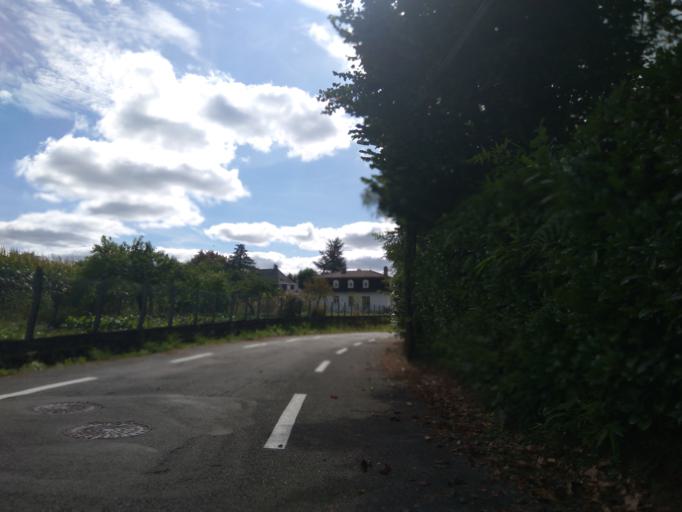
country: FR
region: Aquitaine
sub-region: Departement des Pyrenees-Atlantiques
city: Idron
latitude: 43.2983
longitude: -0.3276
